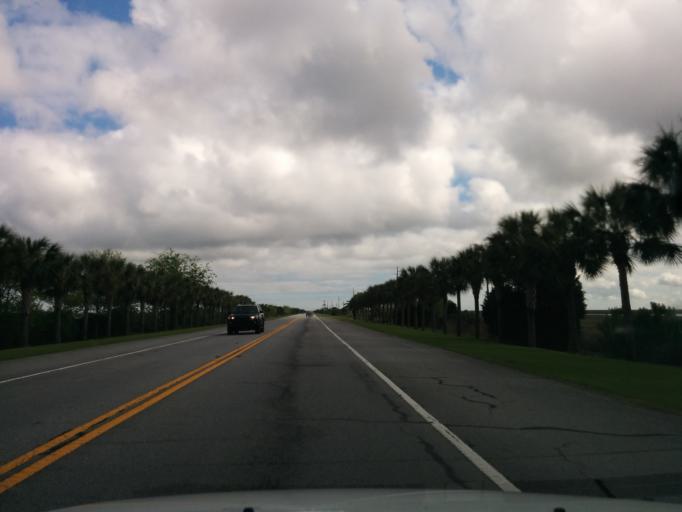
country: US
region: Georgia
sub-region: Glynn County
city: Brunswick
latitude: 31.1032
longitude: -81.4913
